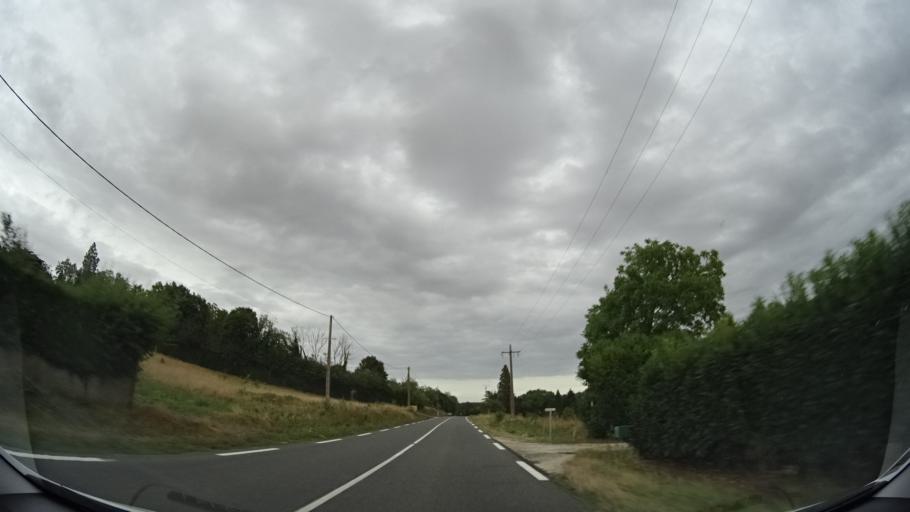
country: FR
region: Centre
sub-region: Departement du Loiret
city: Saint-Germain-des-Pres
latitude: 47.9344
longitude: 2.9003
